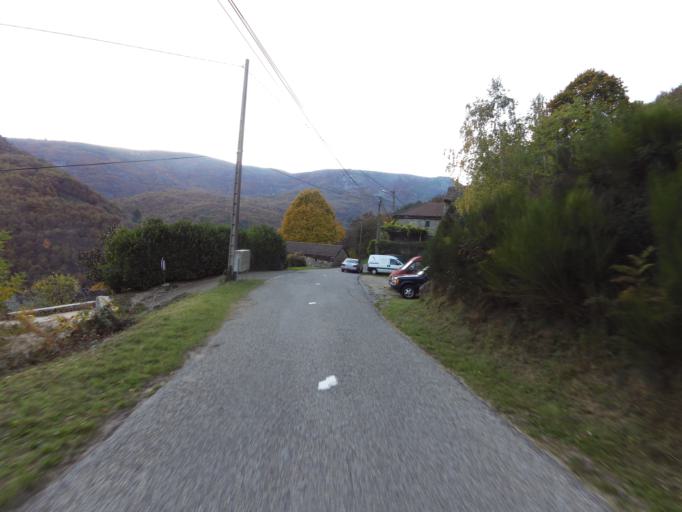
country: FR
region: Rhone-Alpes
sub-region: Departement de l'Ardeche
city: Les Vans
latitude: 44.5336
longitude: 4.0672
